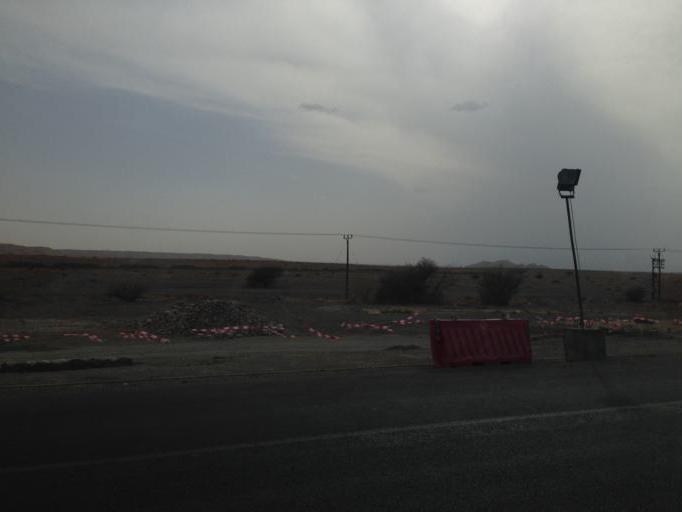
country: OM
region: Ash Sharqiyah
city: Al Qabil
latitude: 22.5397
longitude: 58.7276
